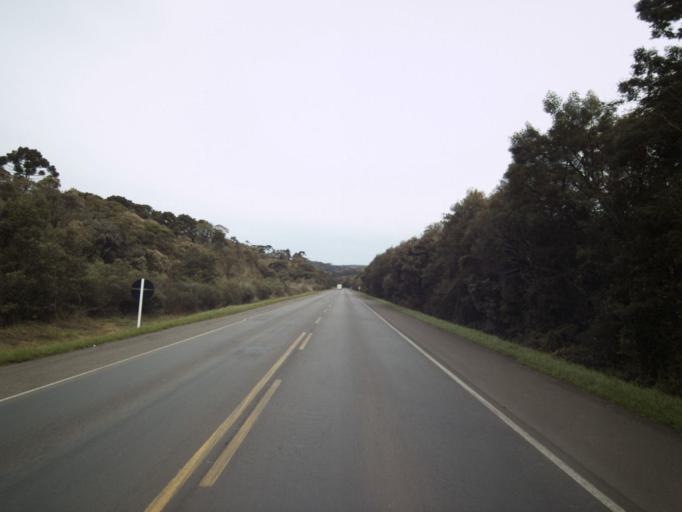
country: BR
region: Parana
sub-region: Palmas
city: Palmas
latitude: -26.6374
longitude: -51.5108
